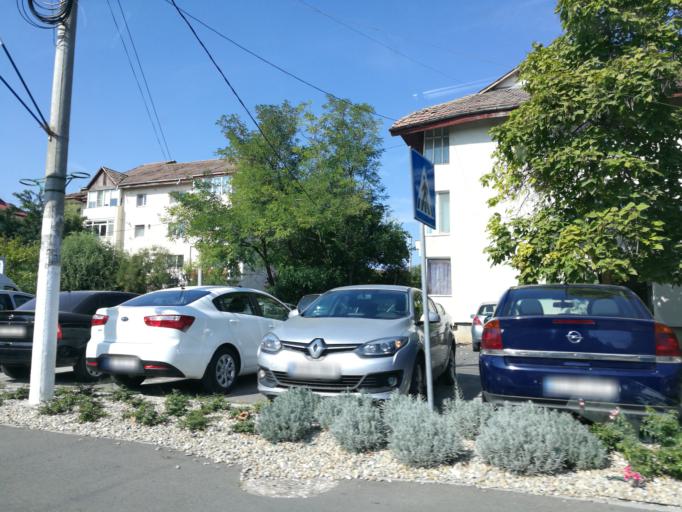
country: RO
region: Ilfov
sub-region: Comuna Otopeni
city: Otopeni
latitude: 44.5511
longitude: 26.0775
